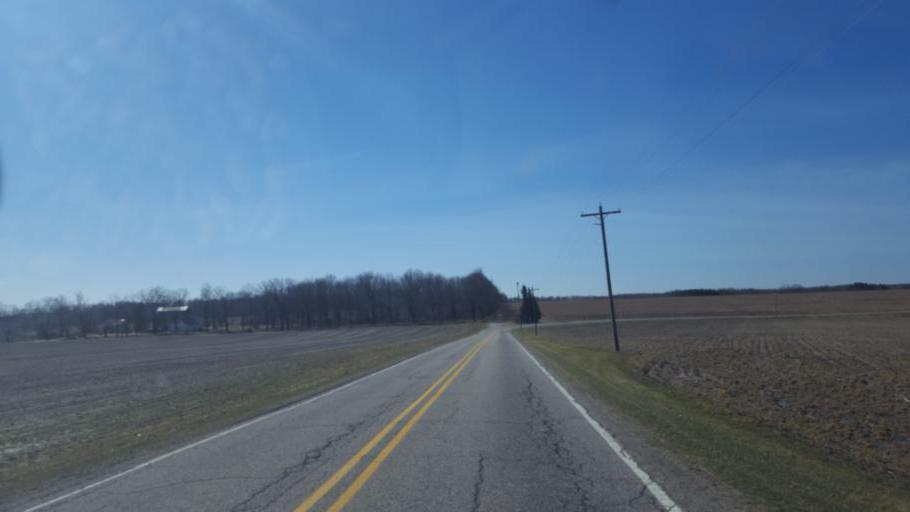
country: US
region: Michigan
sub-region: Montcalm County
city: Edmore
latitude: 43.4903
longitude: -85.0253
